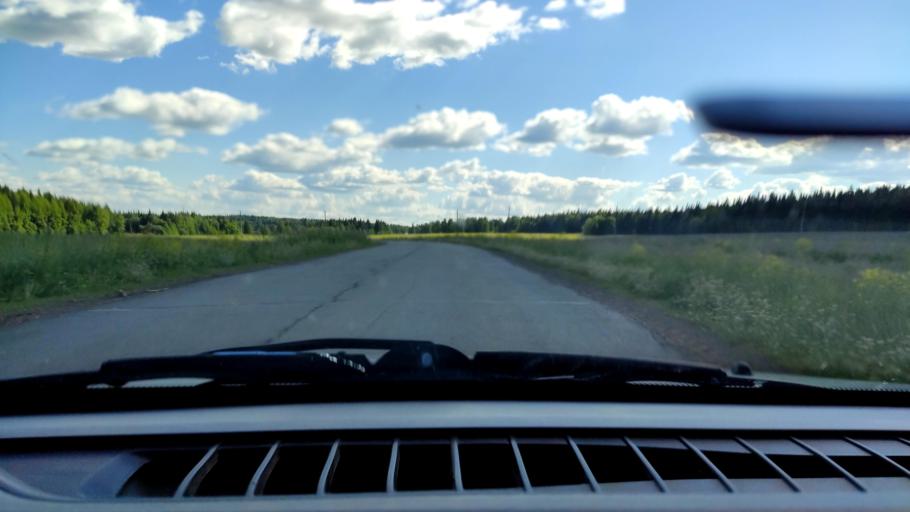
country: RU
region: Perm
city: Uinskoye
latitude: 57.1494
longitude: 56.5702
